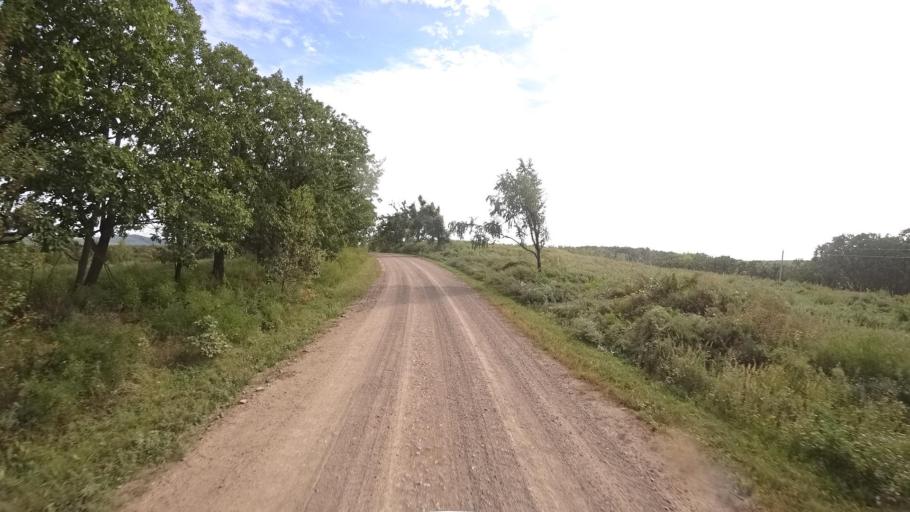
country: RU
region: Primorskiy
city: Dostoyevka
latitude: 44.3603
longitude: 133.5217
